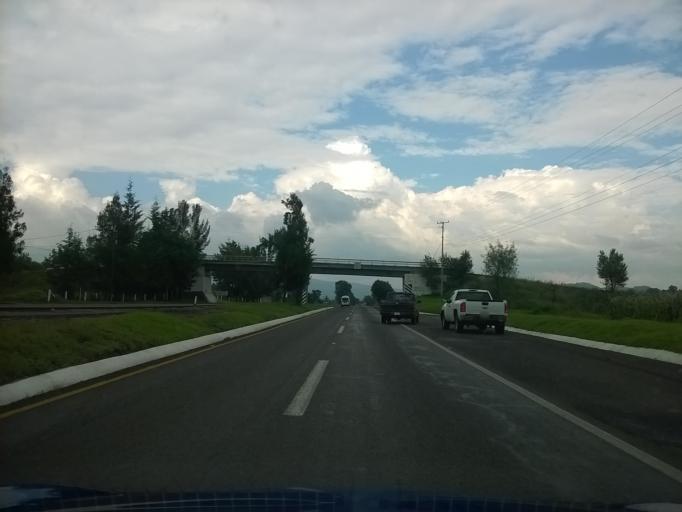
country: MX
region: Michoacan
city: Huiramba
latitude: 19.5376
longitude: -101.4660
